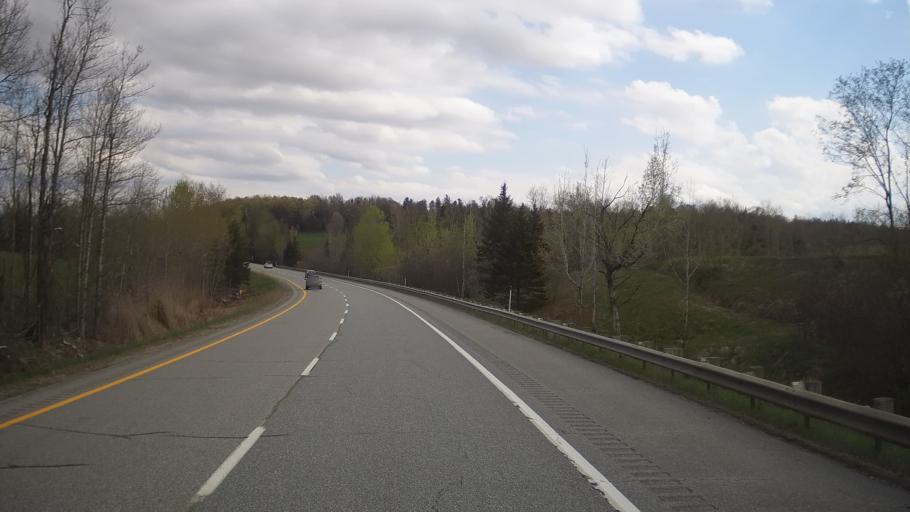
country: CA
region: Quebec
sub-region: Estrie
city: Magog
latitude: 45.1445
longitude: -72.0708
